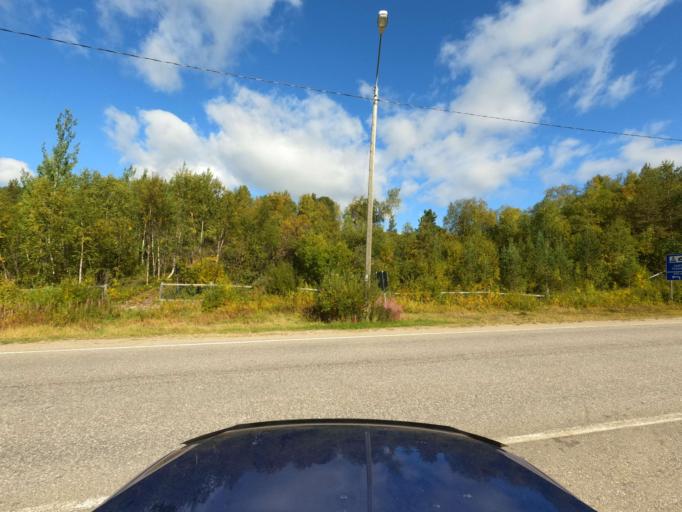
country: NO
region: Finnmark Fylke
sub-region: Karasjok
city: Karasjohka
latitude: 69.3984
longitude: 25.8458
